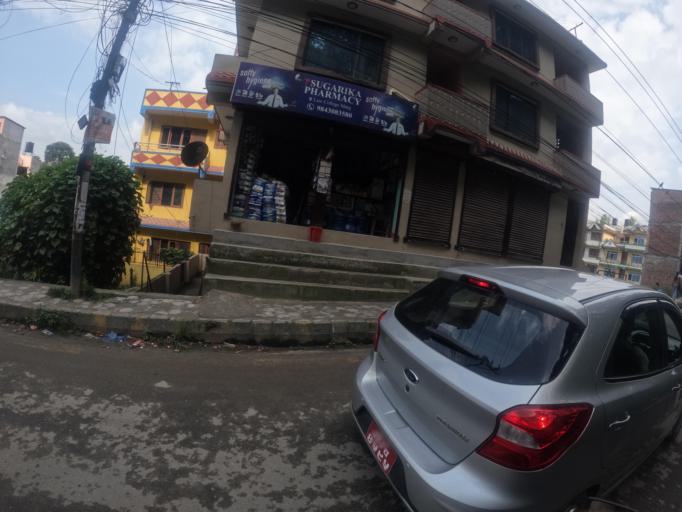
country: NP
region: Central Region
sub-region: Bagmati Zone
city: Bhaktapur
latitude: 27.6657
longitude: 85.3861
